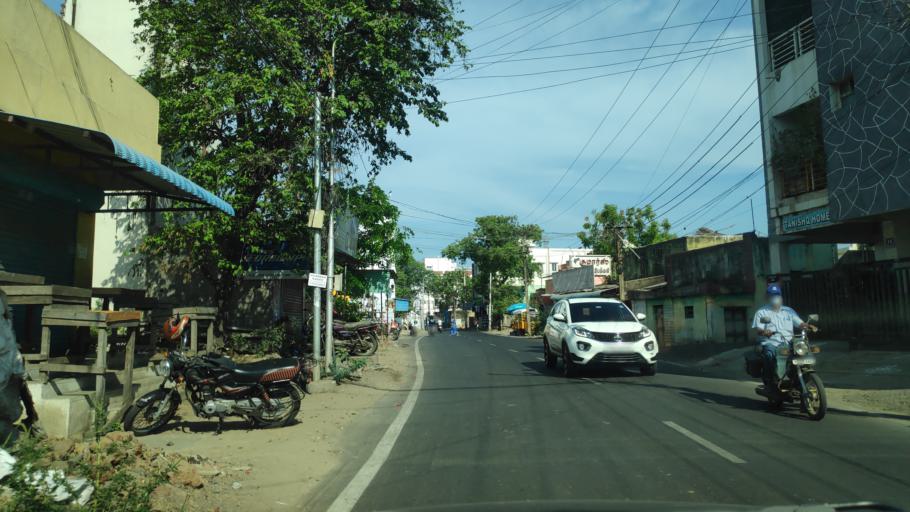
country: IN
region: Tamil Nadu
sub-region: Thiruvallur
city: Ambattur
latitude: 13.1175
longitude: 80.1697
